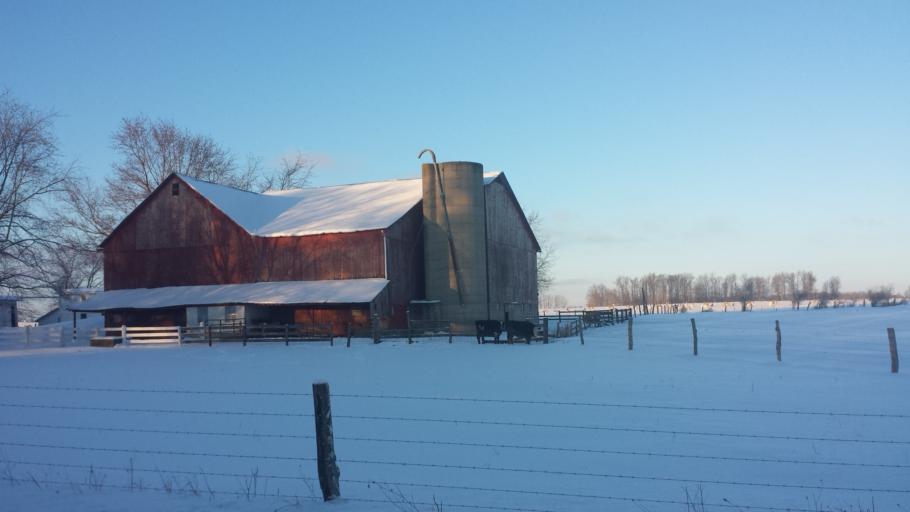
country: US
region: Ohio
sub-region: Ashland County
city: Ashland
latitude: 40.8926
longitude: -82.3875
